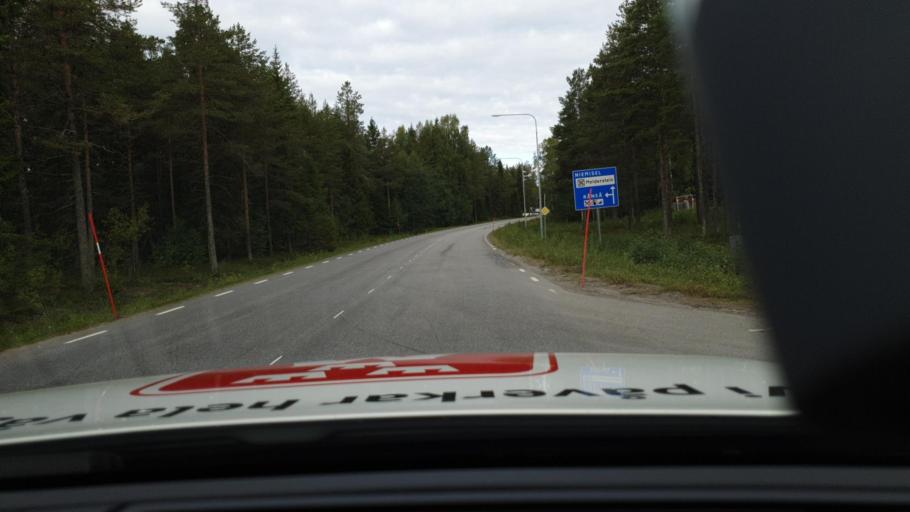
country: SE
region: Norrbotten
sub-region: Lulea Kommun
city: Ranea
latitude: 65.8625
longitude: 22.3123
